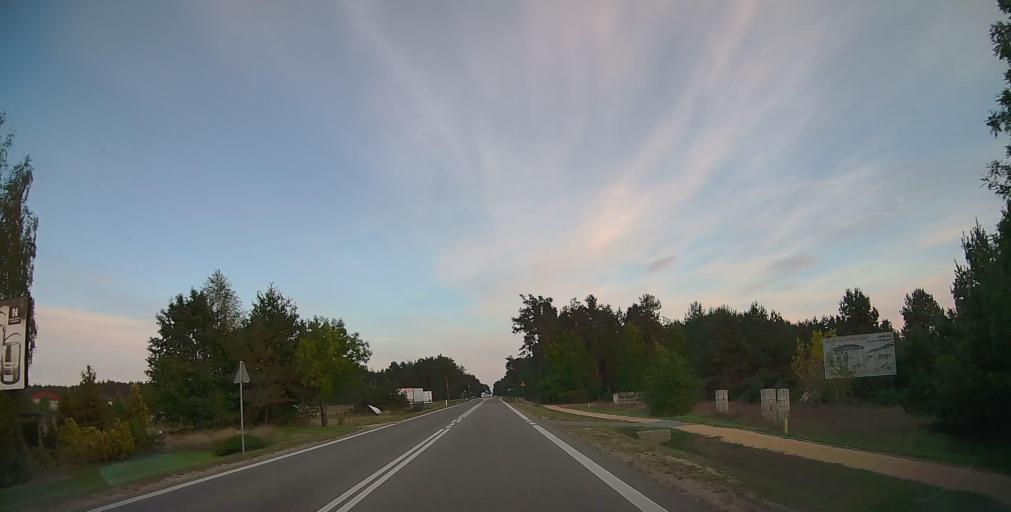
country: PL
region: Masovian Voivodeship
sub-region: Powiat kozienicki
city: Kozienice
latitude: 51.6159
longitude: 21.4935
